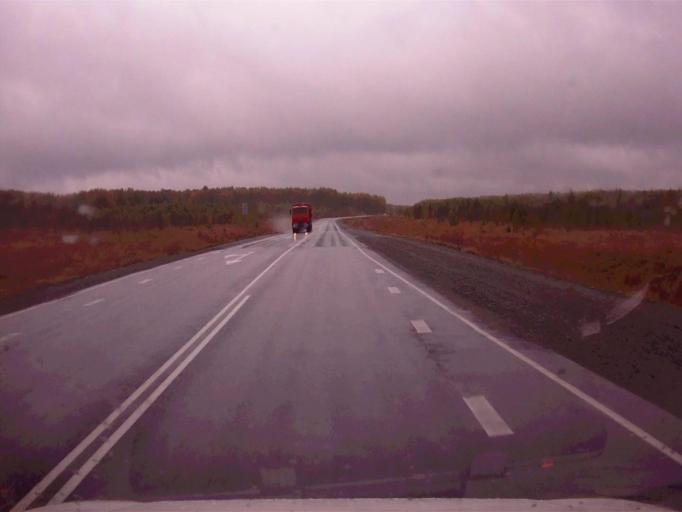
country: RU
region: Chelyabinsk
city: Tayginka
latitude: 55.5042
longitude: 60.6366
